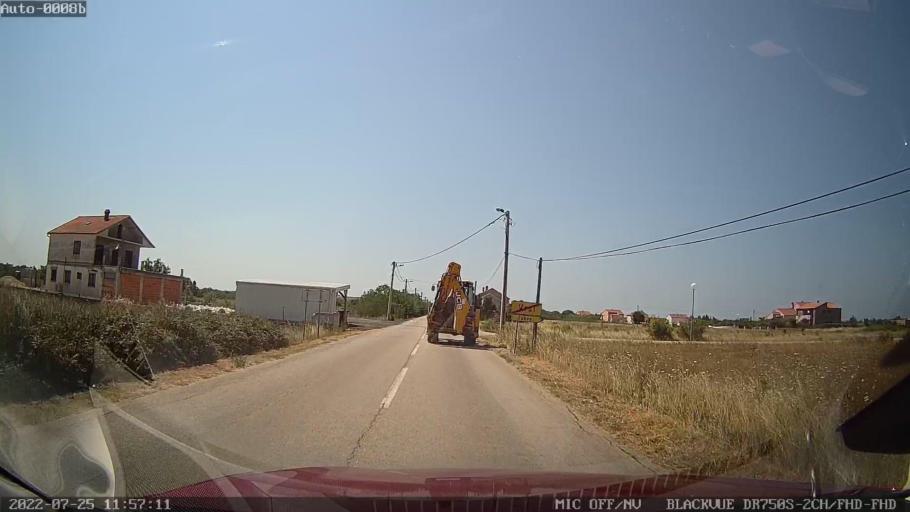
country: HR
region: Zadarska
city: Vrsi
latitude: 44.2450
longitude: 15.2153
